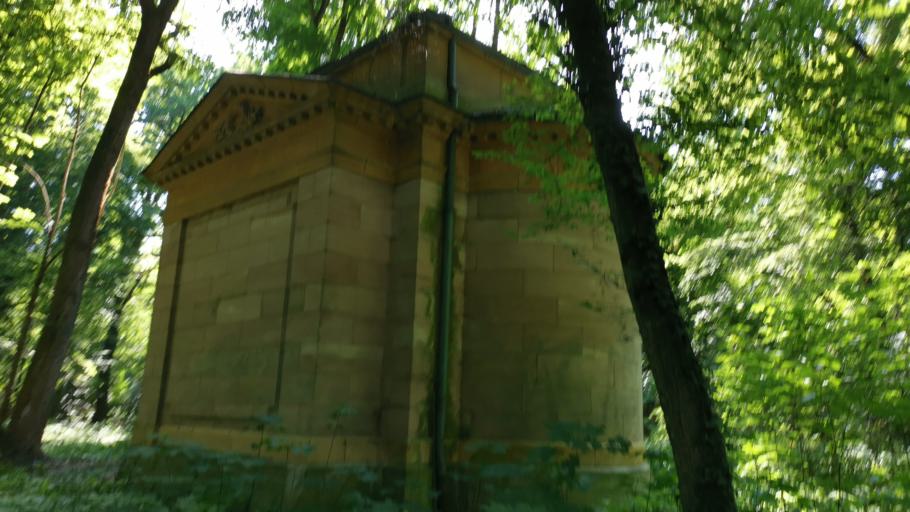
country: DE
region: Bavaria
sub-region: Regierungsbezirk Mittelfranken
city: Stein
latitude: 49.4155
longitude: 11.0255
